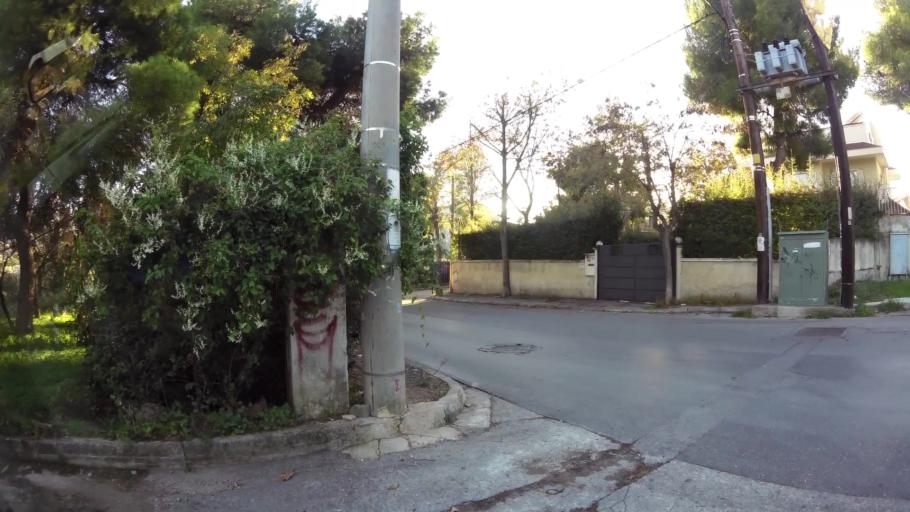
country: GR
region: Attica
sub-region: Nomarchia Anatolikis Attikis
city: Kryoneri
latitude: 38.1364
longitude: 23.8326
